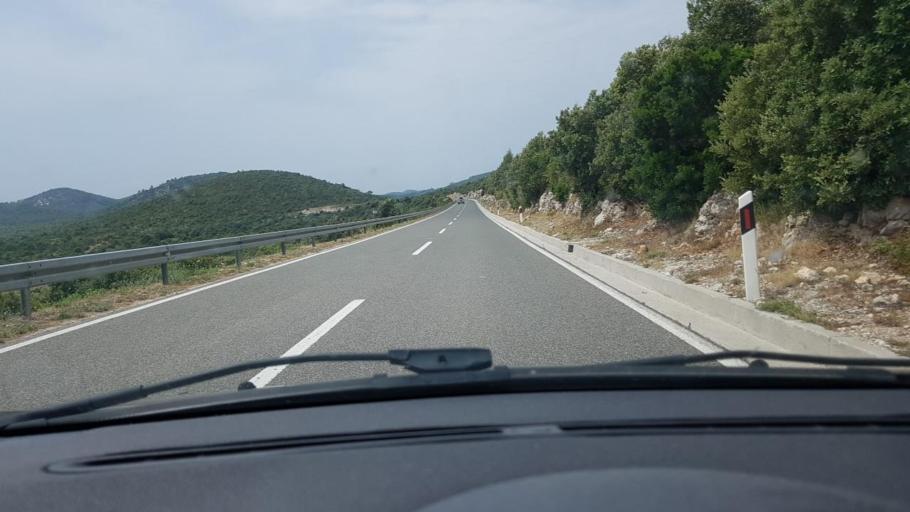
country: HR
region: Dubrovacko-Neretvanska
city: Smokvica
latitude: 42.9552
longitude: 16.9255
